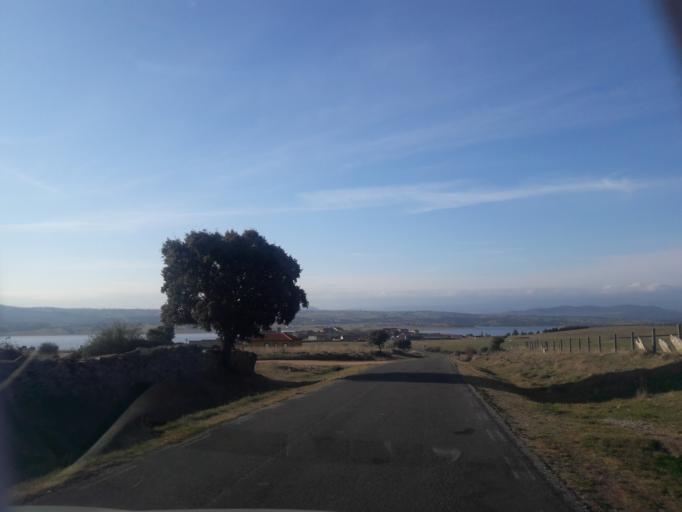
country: ES
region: Castille and Leon
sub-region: Provincia de Salamanca
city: Salvatierra de Tormes
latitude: 40.5971
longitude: -5.5993
